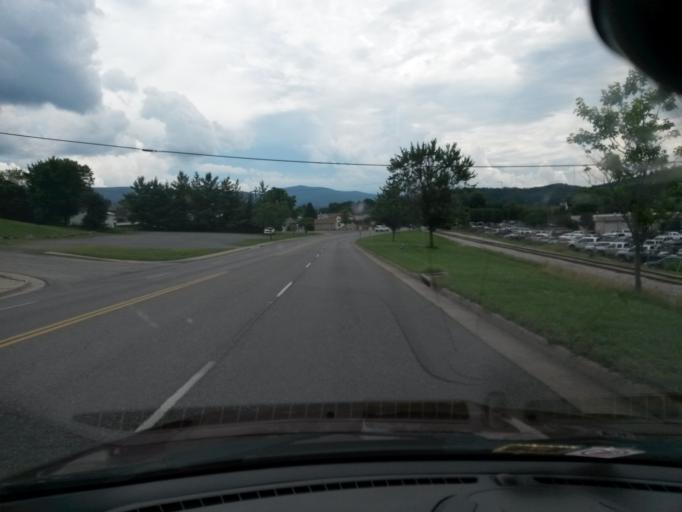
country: US
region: Virginia
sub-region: City of Covington
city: Covington
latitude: 37.7979
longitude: -79.9917
